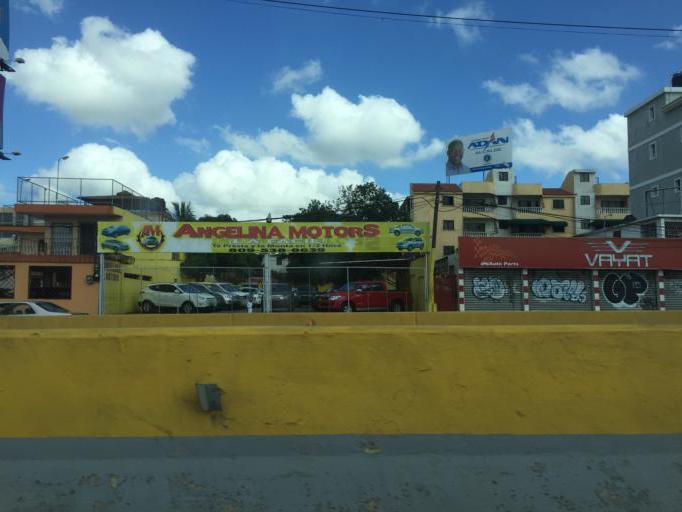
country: DO
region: Santo Domingo
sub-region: Santo Domingo
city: Santo Domingo Este
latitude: 18.4858
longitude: -69.8762
